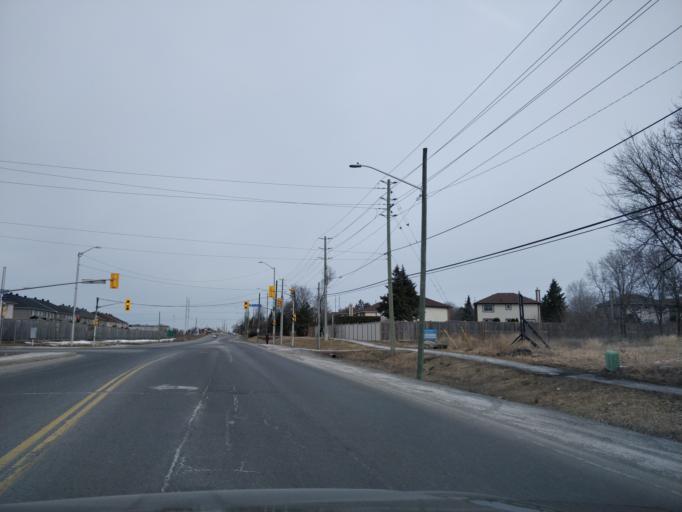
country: CA
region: Ontario
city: Bells Corners
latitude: 45.2777
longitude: -75.8622
